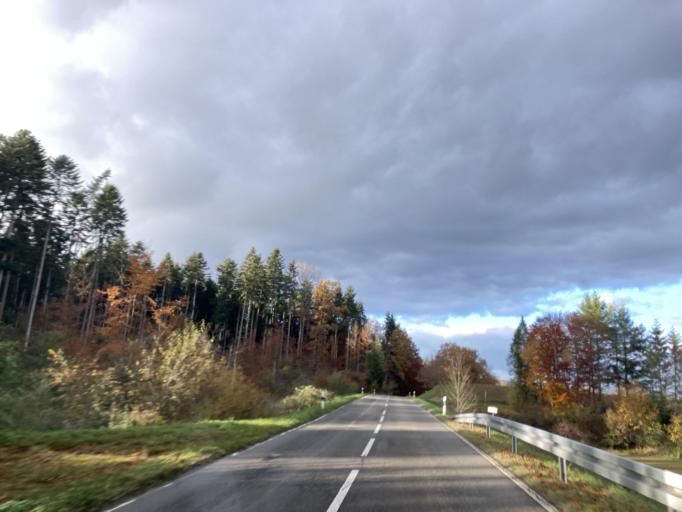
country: DE
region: Baden-Wuerttemberg
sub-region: Karlsruhe Region
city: Empfingen
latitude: 48.4098
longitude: 8.7500
